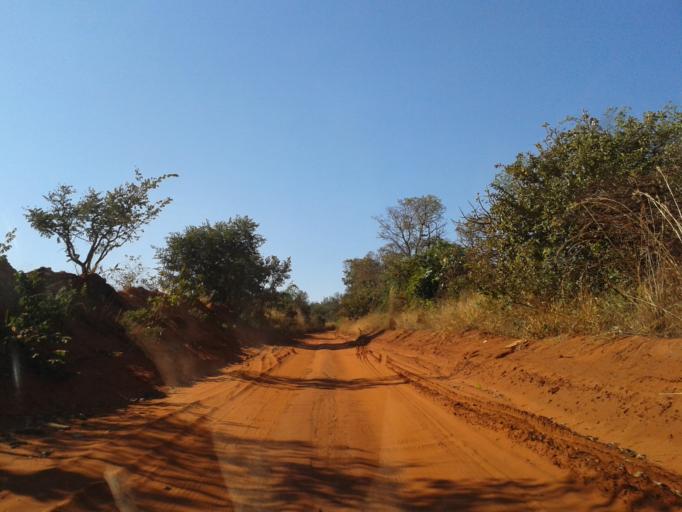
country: BR
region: Minas Gerais
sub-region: Ituiutaba
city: Ituiutaba
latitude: -19.0231
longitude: -49.3509
